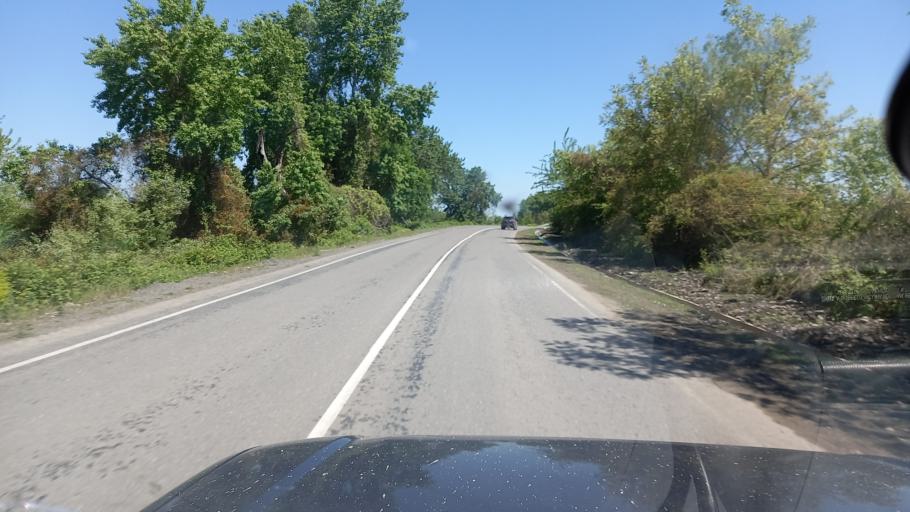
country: RU
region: Dagestan
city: Samur
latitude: 41.7314
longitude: 48.4618
